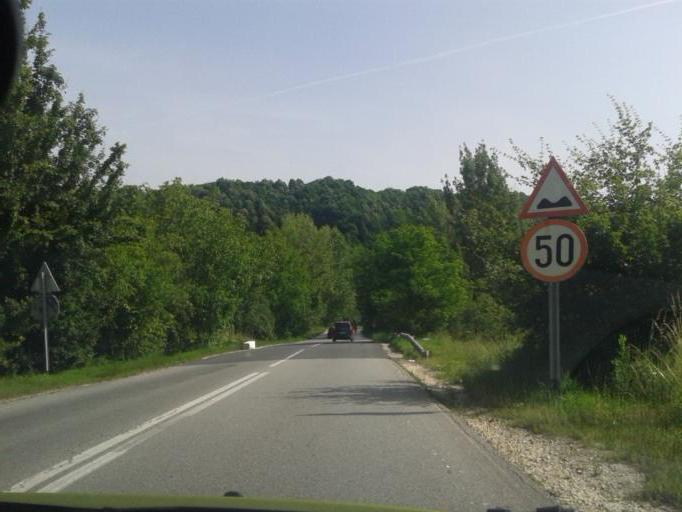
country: RO
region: Valcea
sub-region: Comuna Pietrari
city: Pietrari
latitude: 45.1065
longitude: 24.1365
